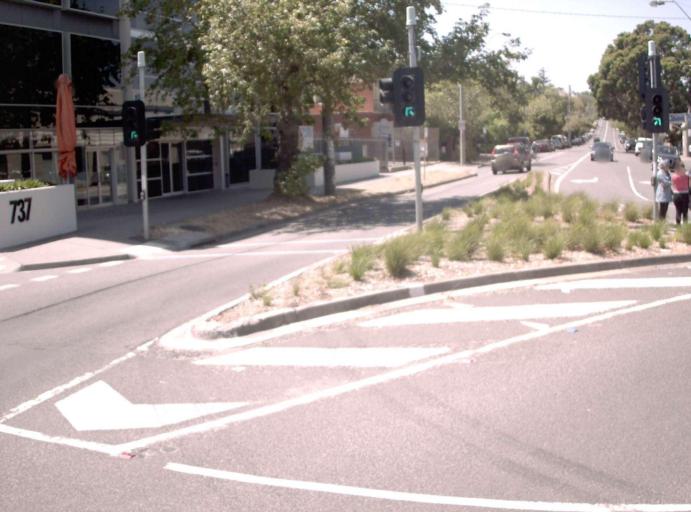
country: AU
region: Victoria
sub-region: Boroondara
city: Hawthorn East
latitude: -37.8242
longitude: 145.0484
